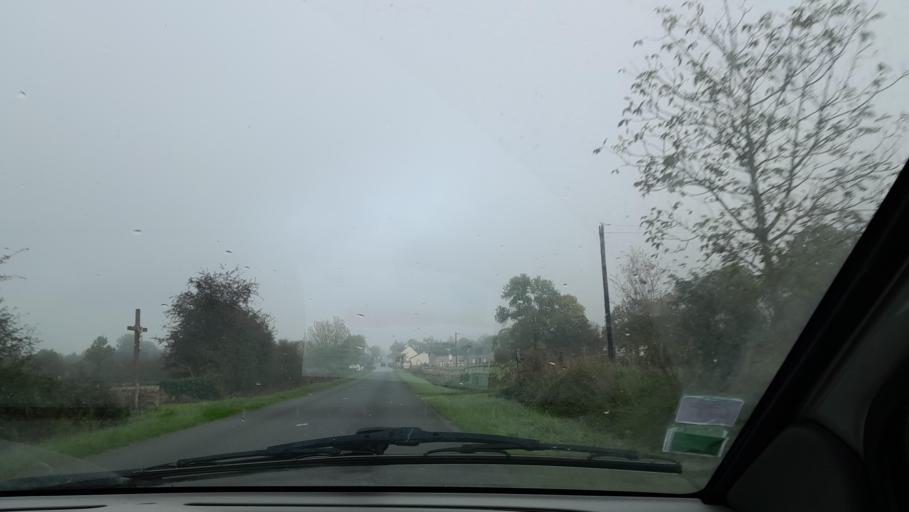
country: FR
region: Pays de la Loire
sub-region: Departement de la Mayenne
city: Saint-Pierre-la-Cour
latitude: 48.1030
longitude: -1.0208
